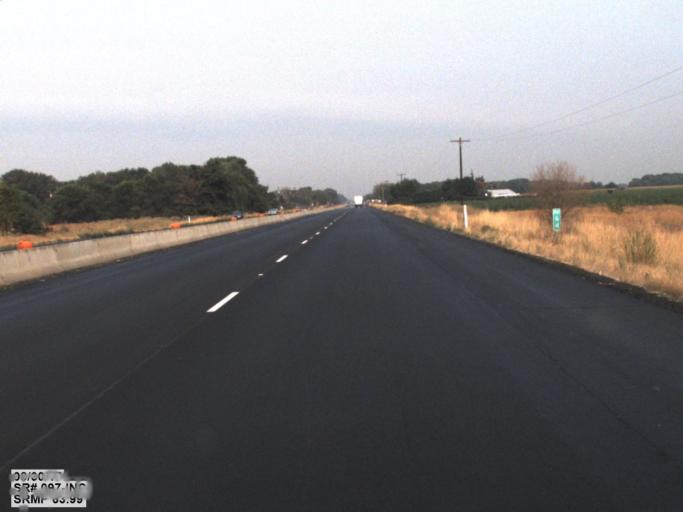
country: US
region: Washington
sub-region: Yakima County
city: Toppenish
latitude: 46.3925
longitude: -120.3626
